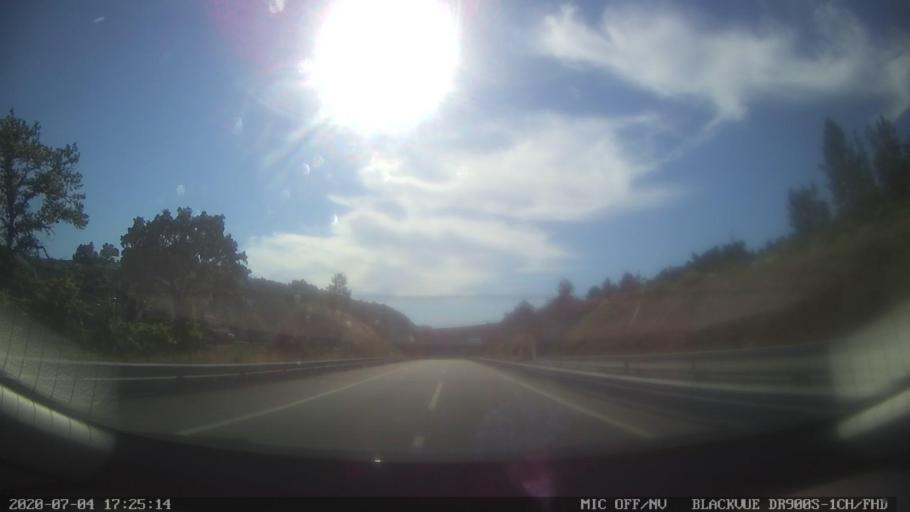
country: PT
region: Porto
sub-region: Amarante
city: Amarante
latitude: 41.2549
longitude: -8.0508
